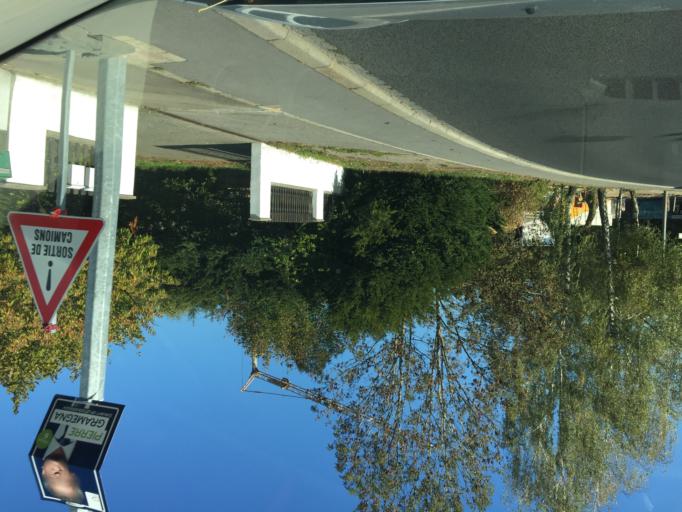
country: LU
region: Luxembourg
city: Bridel
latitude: 49.6599
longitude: 6.0810
